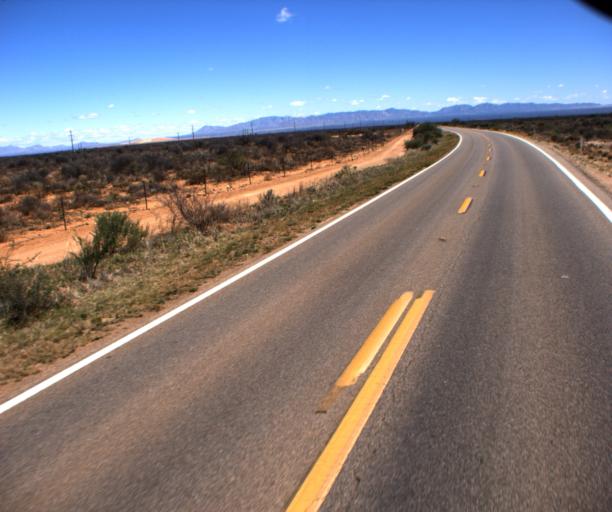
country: US
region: Arizona
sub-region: Cochise County
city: Huachuca City
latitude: 31.6961
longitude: -110.3066
